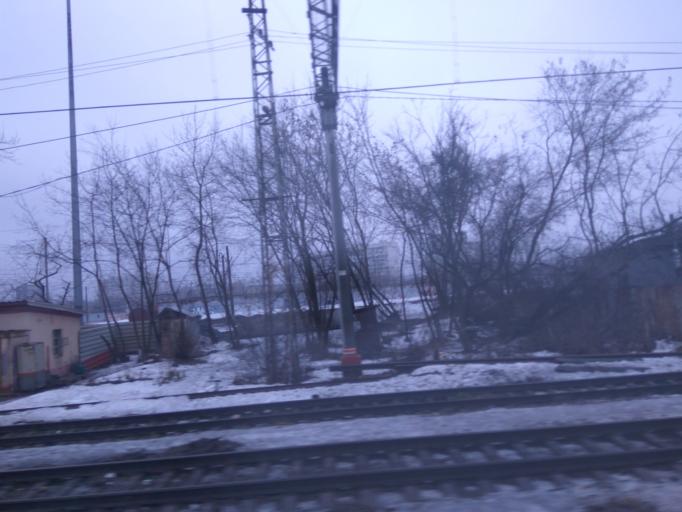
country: RU
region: Moscow
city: Mar'ina Roshcha
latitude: 55.8014
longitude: 37.6276
